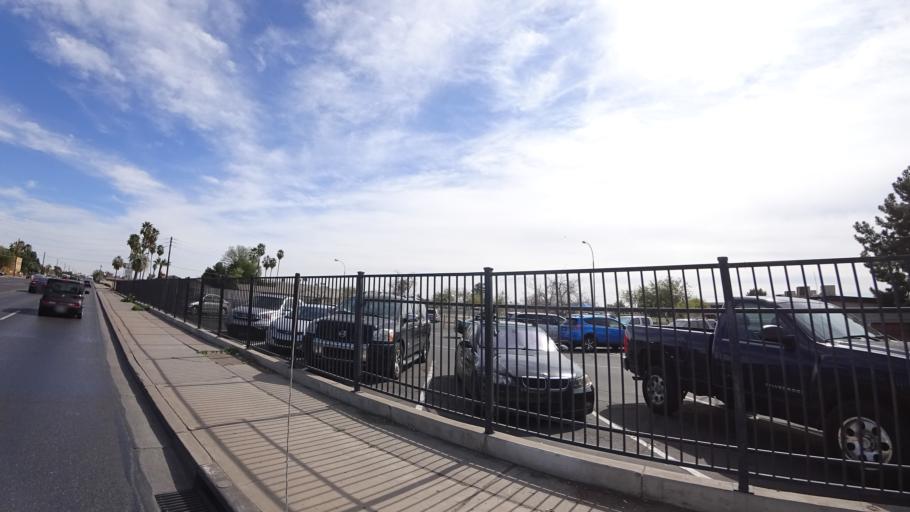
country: US
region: Arizona
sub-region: Maricopa County
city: Glendale
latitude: 33.4805
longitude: -112.1850
